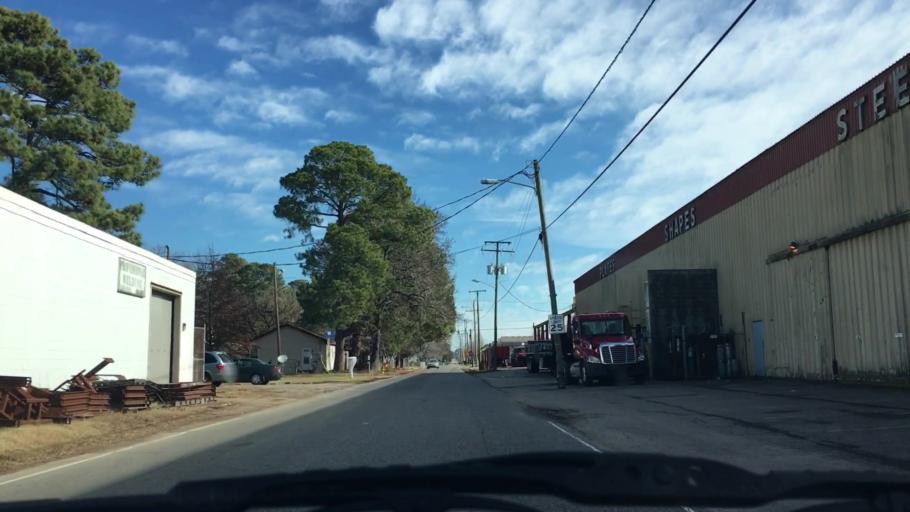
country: US
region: Virginia
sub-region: City of Norfolk
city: Norfolk
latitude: 36.8651
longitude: -76.2451
